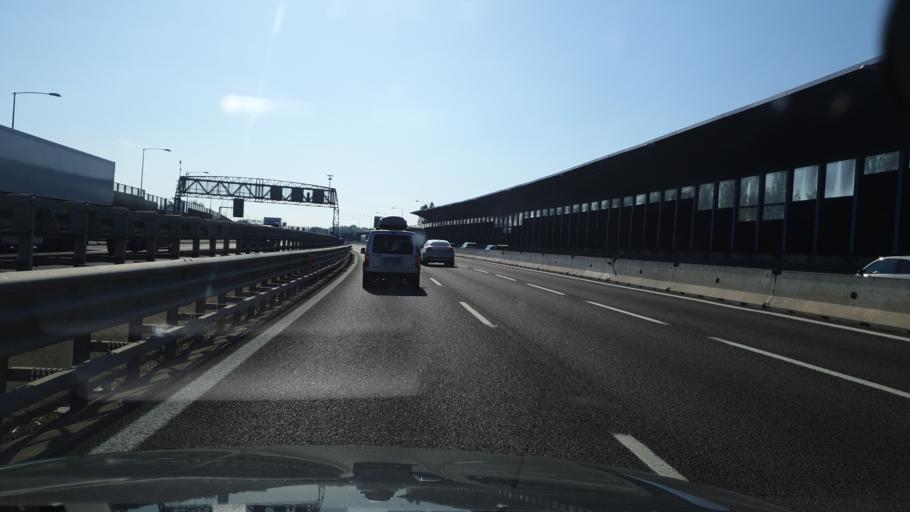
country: IT
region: Emilia-Romagna
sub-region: Provincia di Bologna
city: San Lazzaro
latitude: 44.4897
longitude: 11.3954
